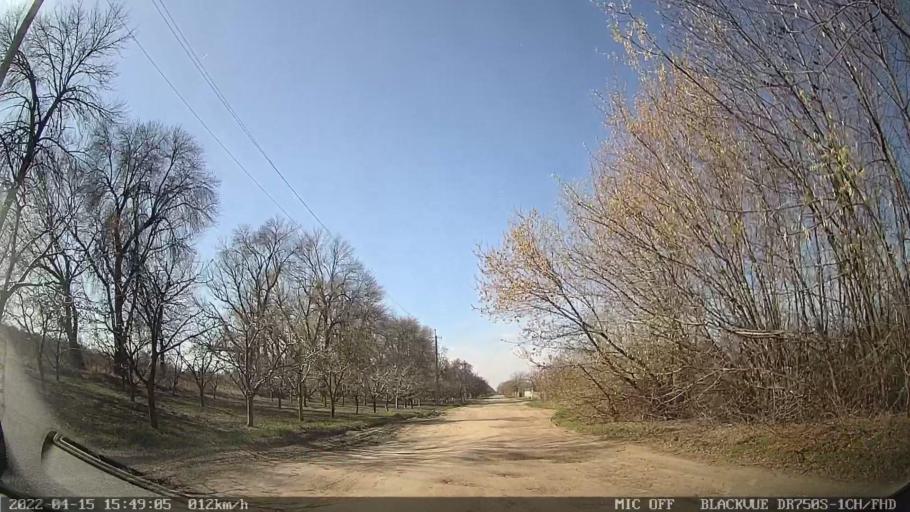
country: MD
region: Raionul Ocnita
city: Otaci
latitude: 48.3884
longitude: 27.9051
